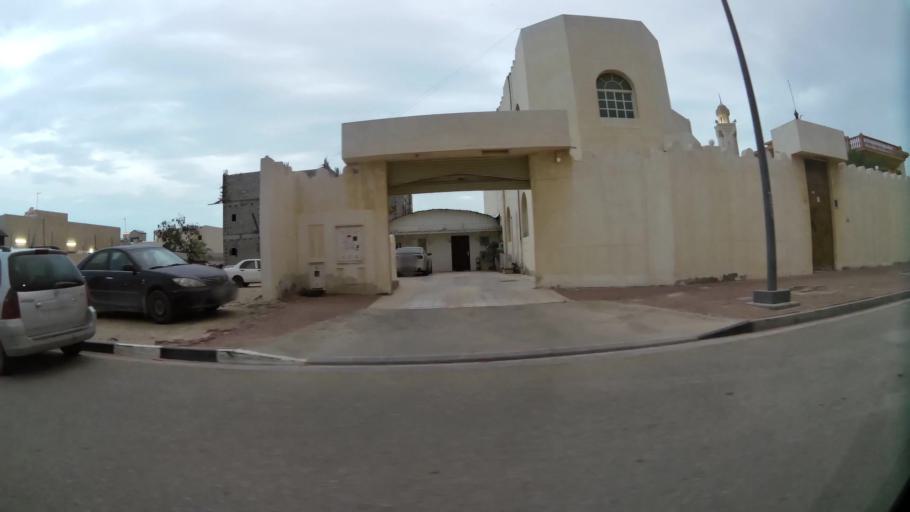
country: QA
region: Baladiyat ad Dawhah
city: Doha
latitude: 25.3483
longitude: 51.5120
